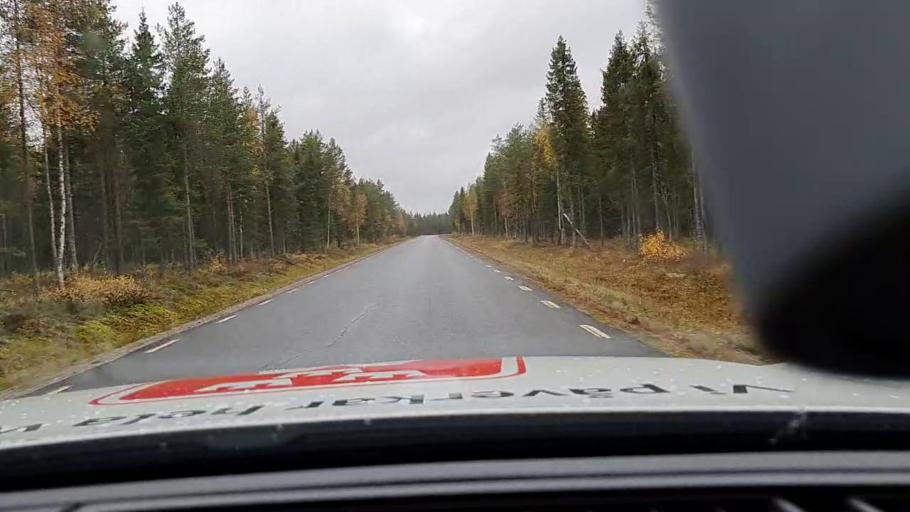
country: SE
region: Norrbotten
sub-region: Haparanda Kommun
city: Haparanda
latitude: 65.9368
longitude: 23.8086
